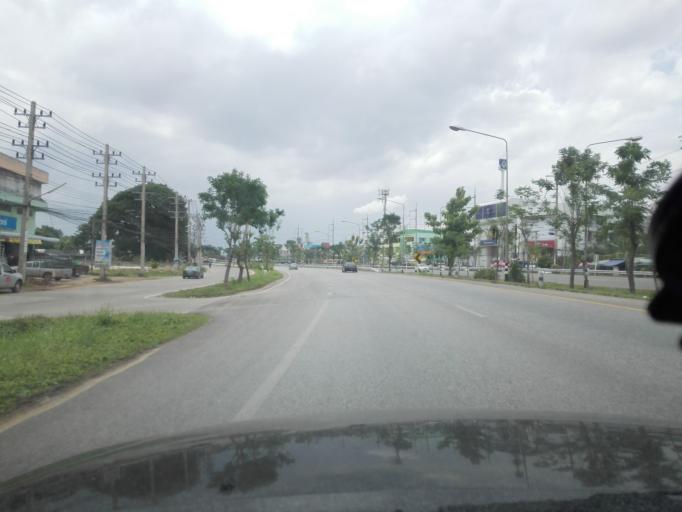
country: TH
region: Kamphaeng Phet
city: Kamphaeng Phet
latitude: 16.4789
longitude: 99.4961
